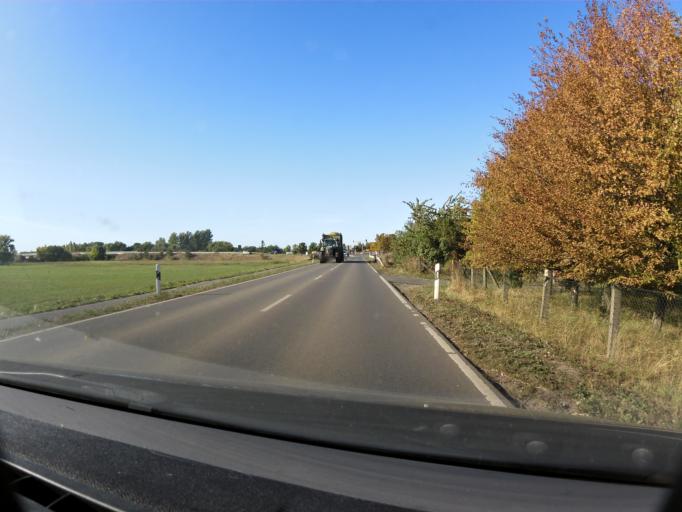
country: DE
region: Saxony-Anhalt
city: Groeningen
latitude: 51.9442
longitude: 11.2124
